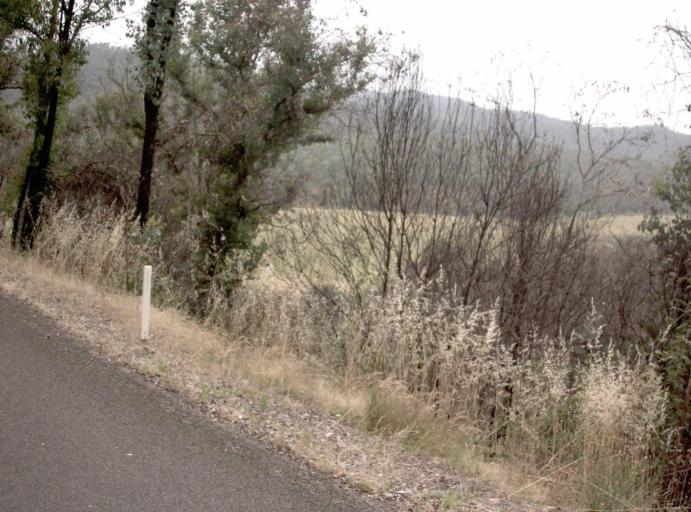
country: AU
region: Victoria
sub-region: Wellington
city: Heyfield
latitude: -37.8126
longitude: 146.6719
